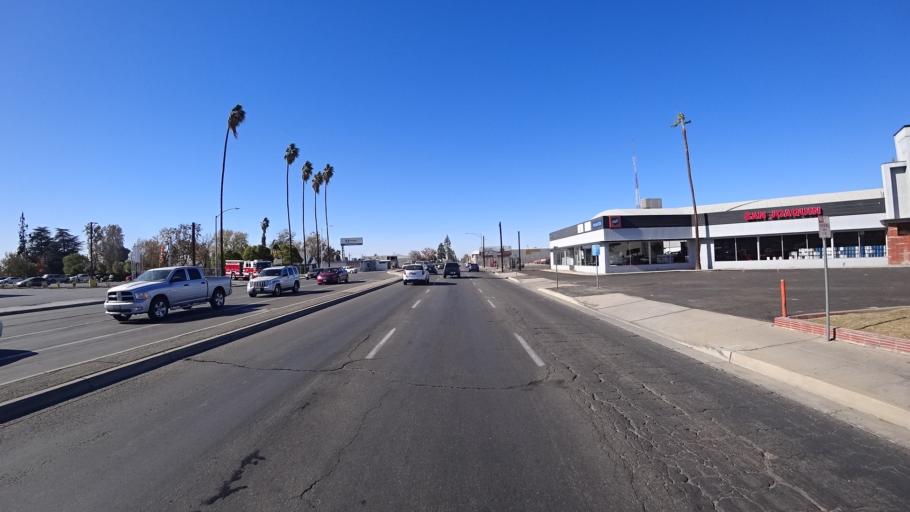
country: US
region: California
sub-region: Kern County
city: Bakersfield
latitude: 35.3685
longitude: -119.0033
